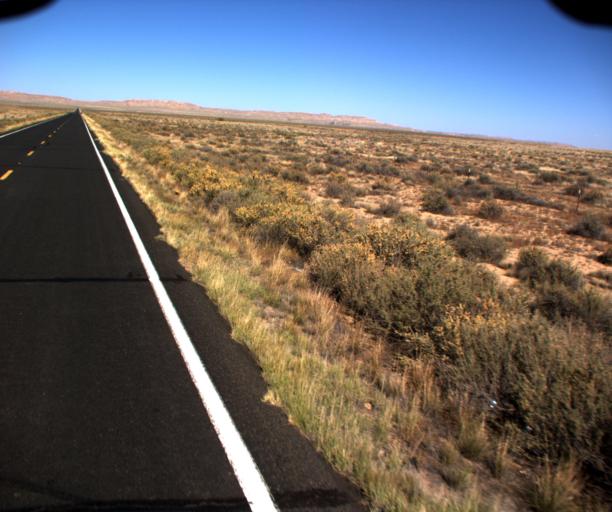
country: US
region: Arizona
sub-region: Navajo County
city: First Mesa
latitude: 35.7030
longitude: -110.5085
